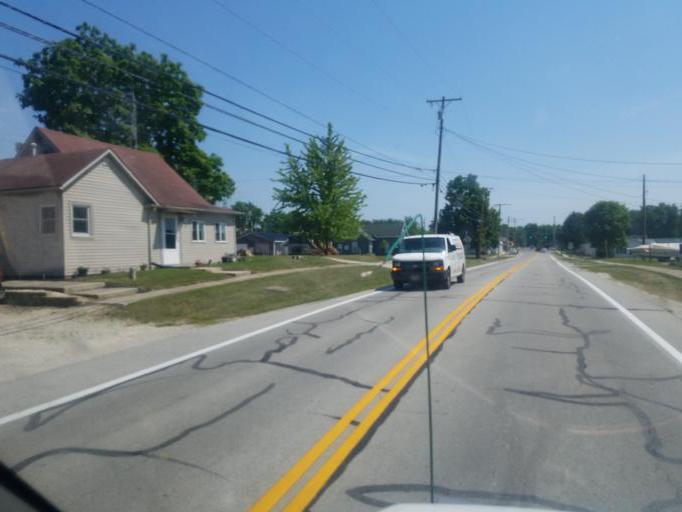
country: US
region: Ohio
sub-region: Mercer County
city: Celina
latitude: 40.4910
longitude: -84.5494
